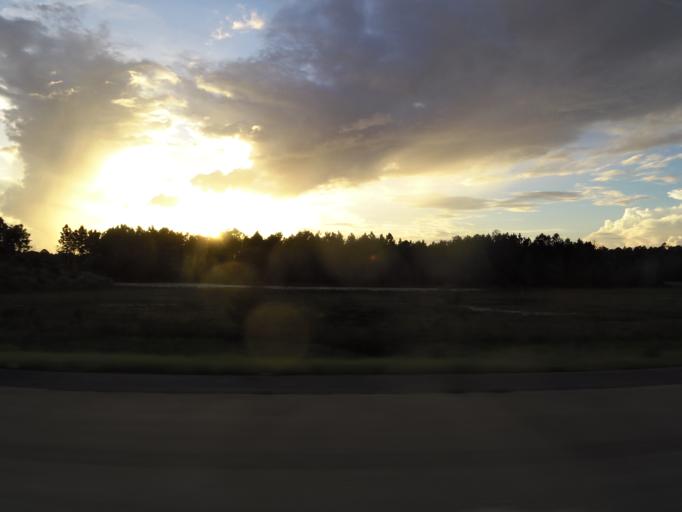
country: US
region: Georgia
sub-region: Glynn County
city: Dock Junction
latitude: 31.2403
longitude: -81.5053
